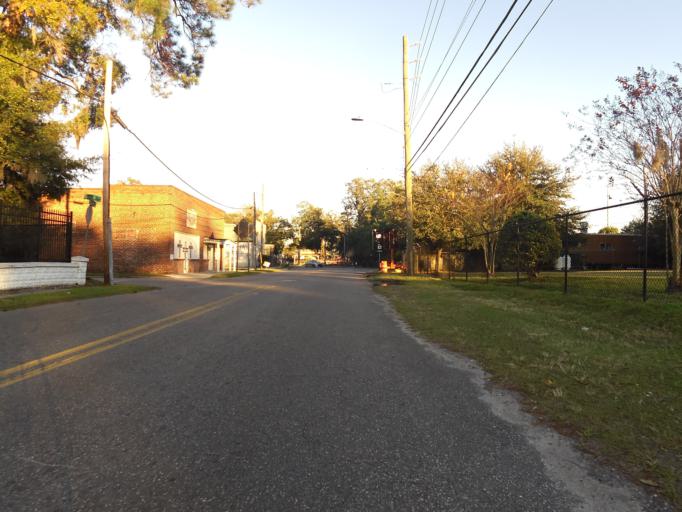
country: US
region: Florida
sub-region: Duval County
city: Jacksonville
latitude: 30.3226
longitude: -81.6977
